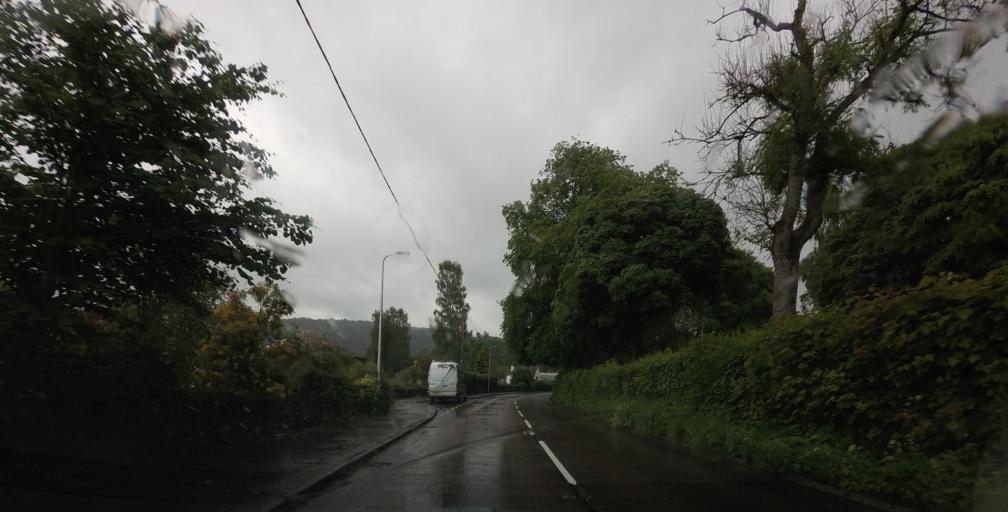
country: GB
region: Scotland
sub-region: Perth and Kinross
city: Bankfoot
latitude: 56.5607
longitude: -3.5815
